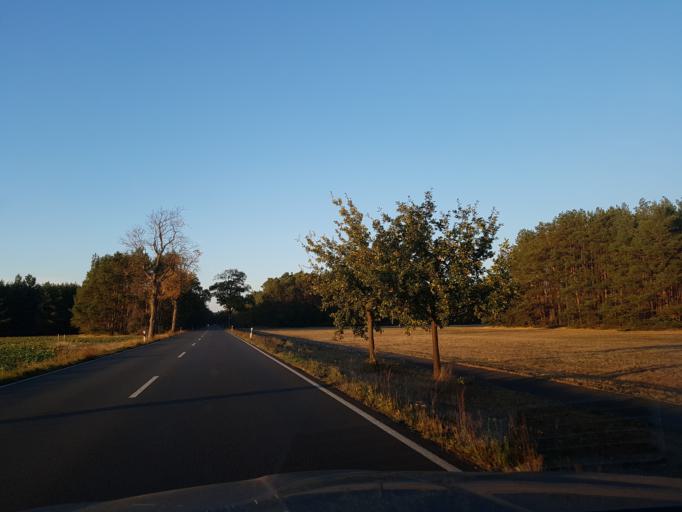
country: DE
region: Brandenburg
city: Schilda
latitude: 51.5800
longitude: 13.3574
